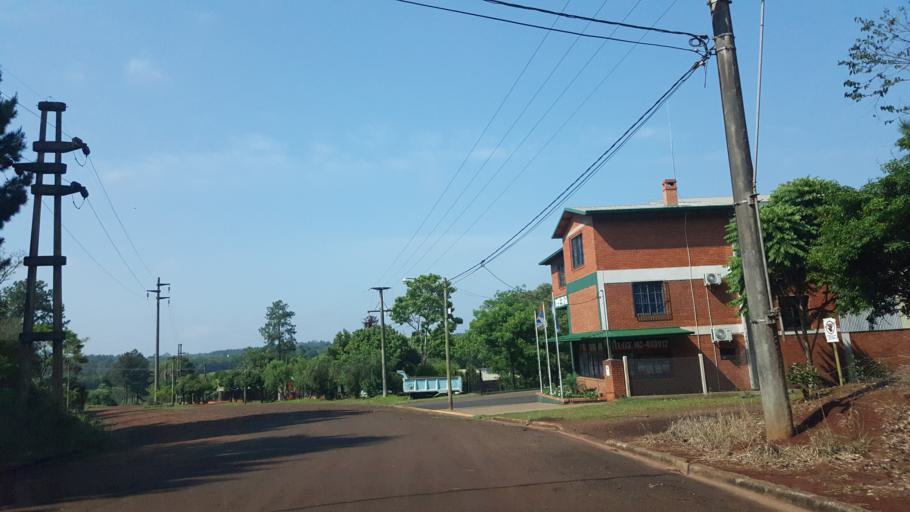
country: AR
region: Misiones
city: Capiovi
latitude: -26.9340
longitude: -55.0653
